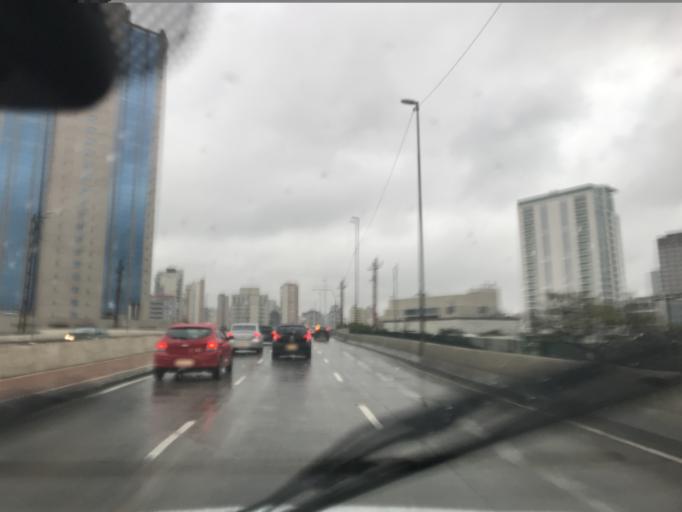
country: BR
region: Sao Paulo
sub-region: Sao Paulo
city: Sao Paulo
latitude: -23.5246
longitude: -46.6708
